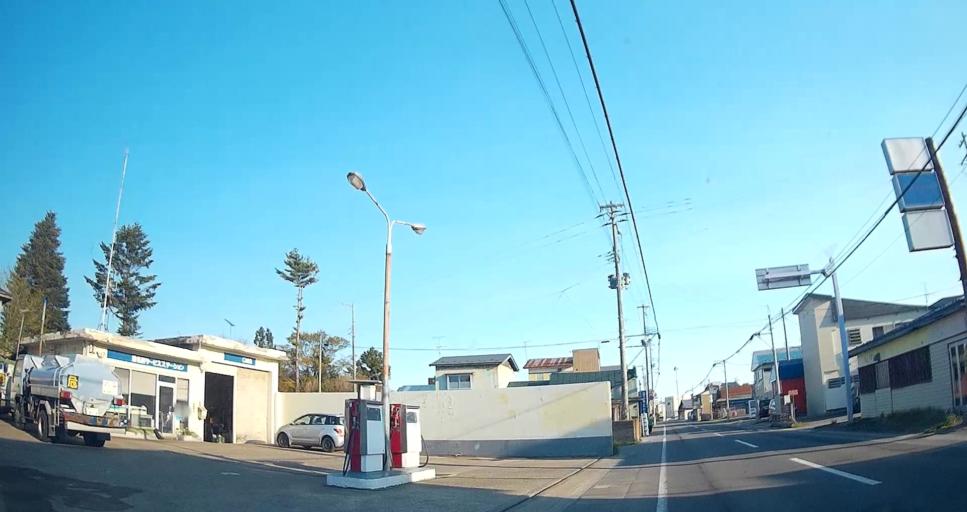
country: JP
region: Aomori
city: Mutsu
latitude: 41.2908
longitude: 141.2109
